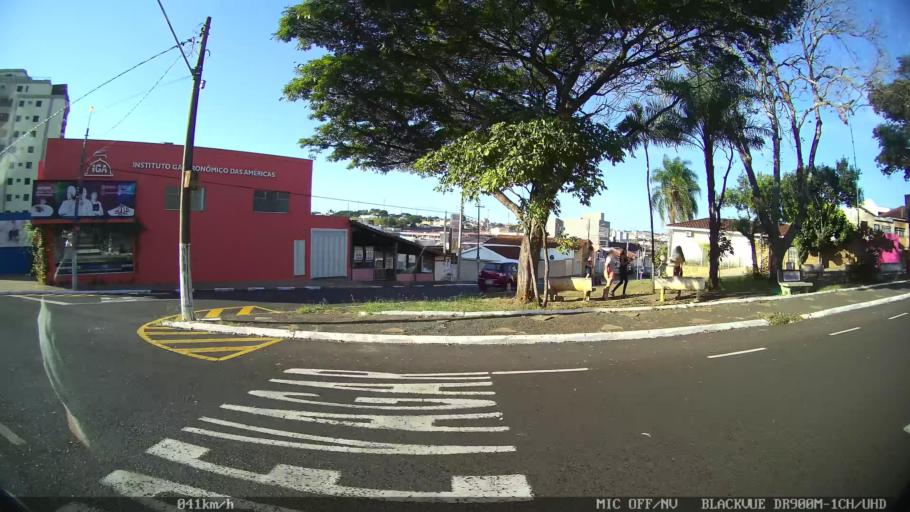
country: BR
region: Sao Paulo
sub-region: Franca
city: Franca
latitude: -20.5398
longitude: -47.3882
